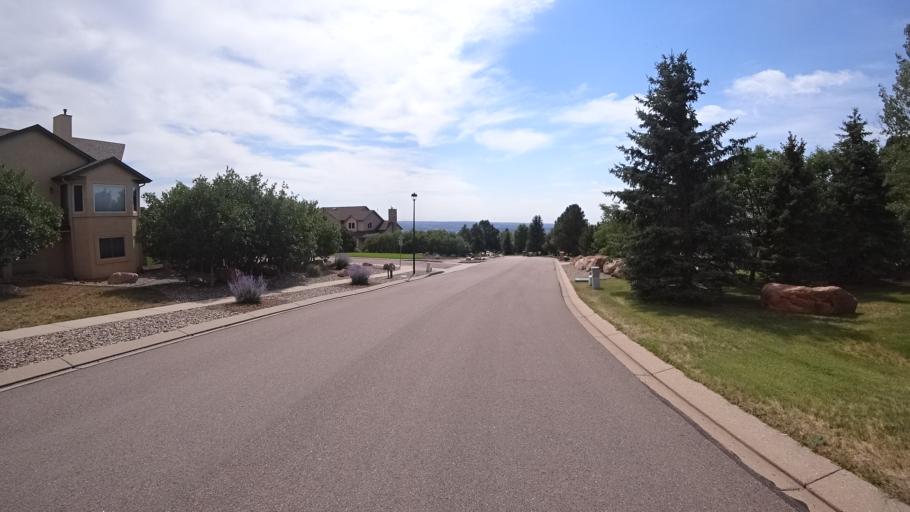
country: US
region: Colorado
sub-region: El Paso County
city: Air Force Academy
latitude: 38.9537
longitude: -104.8861
